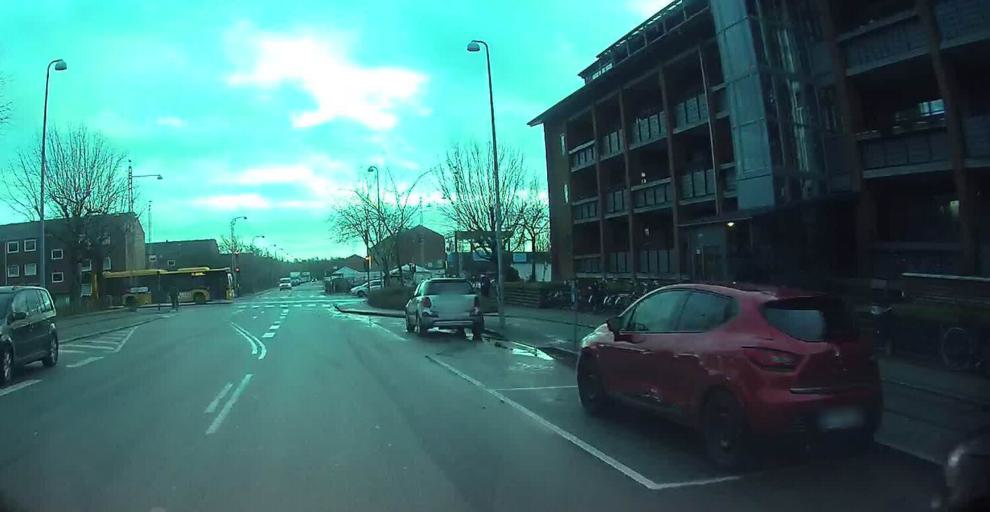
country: DK
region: Capital Region
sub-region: Tarnby Kommune
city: Tarnby
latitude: 55.6349
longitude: 12.6100
